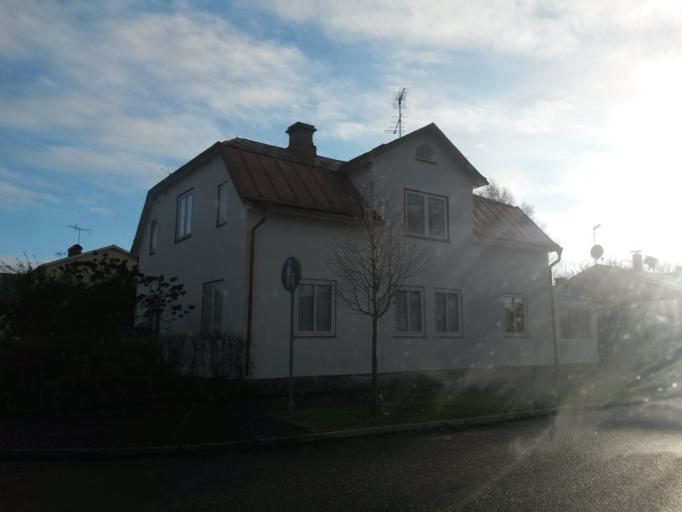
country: SE
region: Vaestra Goetaland
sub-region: Grastorps Kommun
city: Graestorp
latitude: 58.3339
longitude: 12.6854
